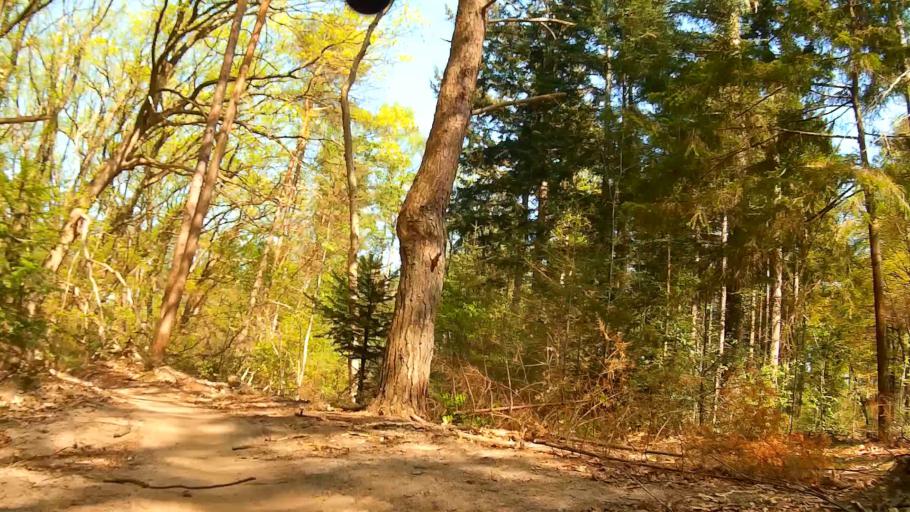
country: NL
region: Utrecht
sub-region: Gemeente Baarn
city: Baarn
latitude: 52.1947
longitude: 5.2571
